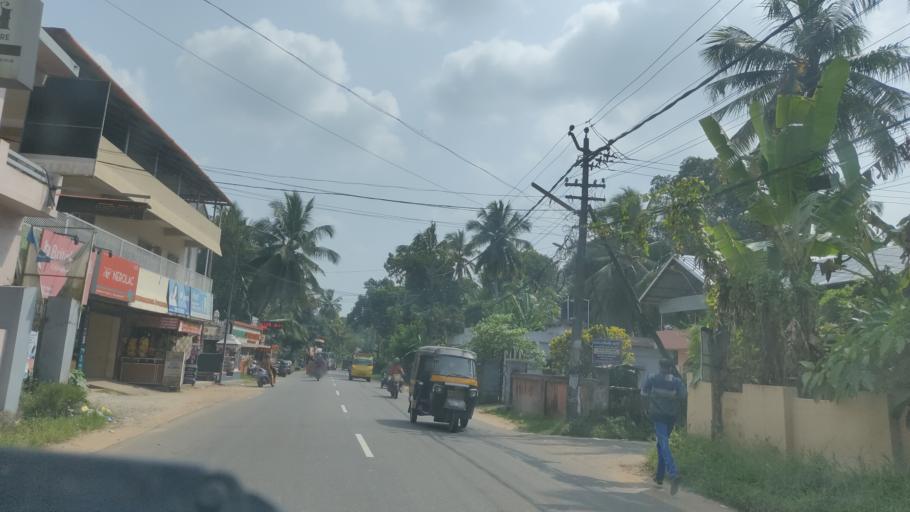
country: IN
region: Kerala
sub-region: Pattanamtitta
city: Tiruvalla
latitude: 9.3368
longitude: 76.5345
